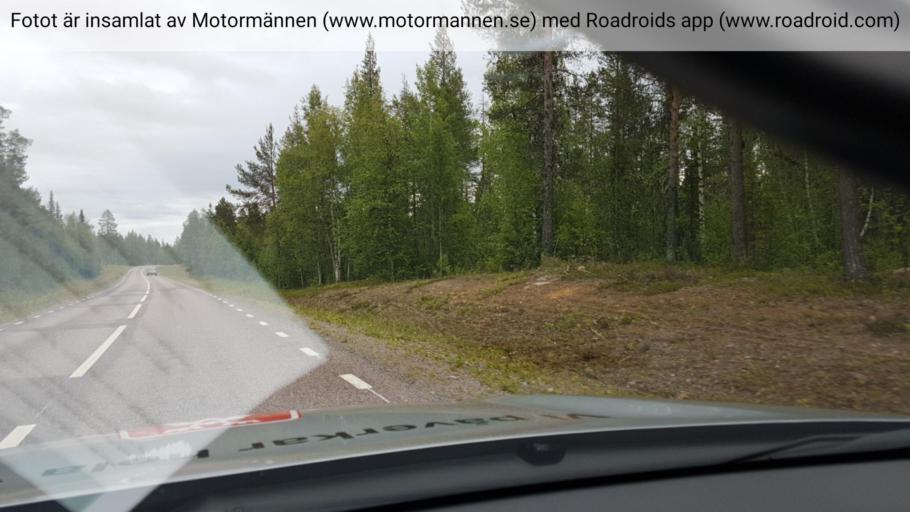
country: SE
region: Norrbotten
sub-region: Gallivare Kommun
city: Gaellivare
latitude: 67.0636
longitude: 21.5679
